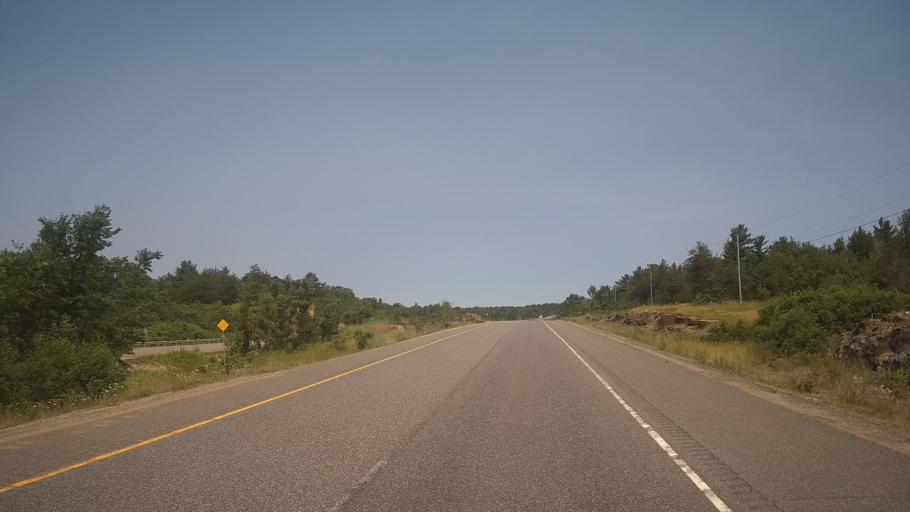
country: CA
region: Ontario
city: Midland
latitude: 44.9027
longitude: -79.7697
